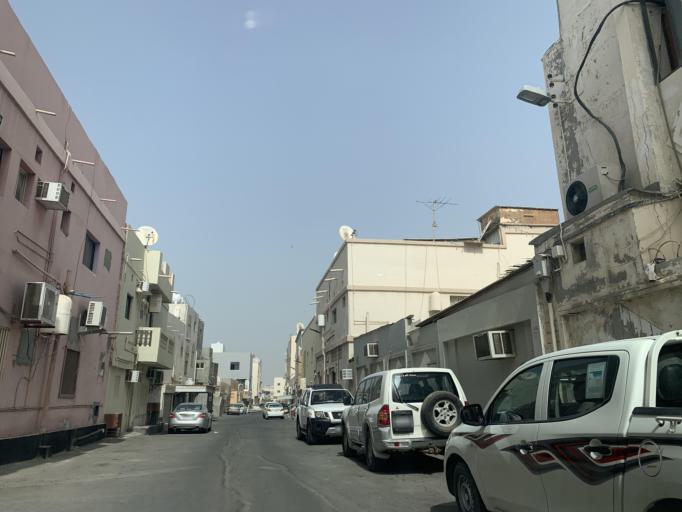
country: BH
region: Northern
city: Madinat `Isa
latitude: 26.1577
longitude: 50.5172
